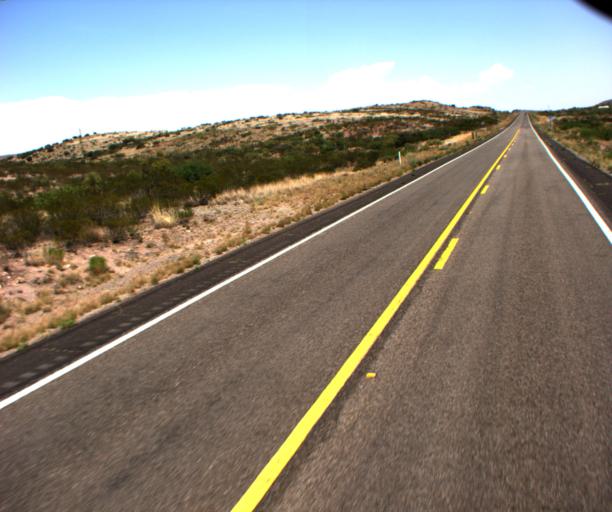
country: US
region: Arizona
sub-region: Greenlee County
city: Clifton
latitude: 32.7772
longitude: -109.2919
